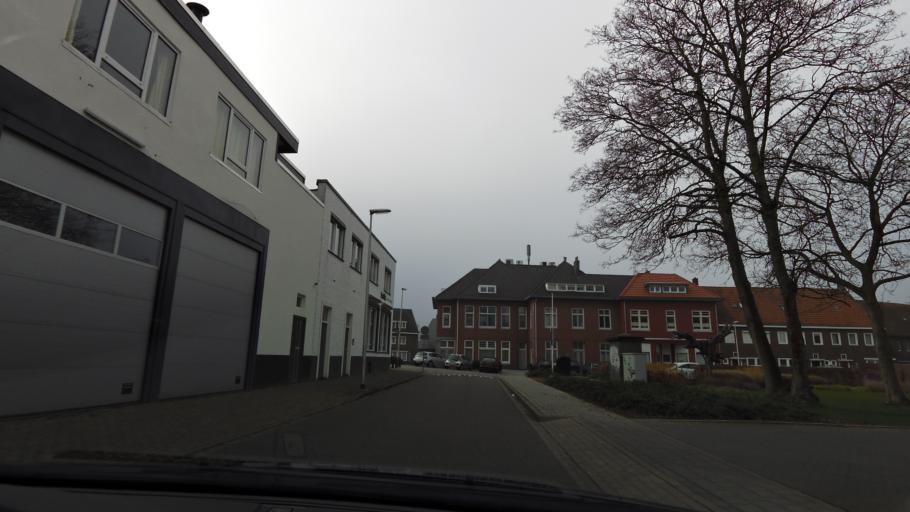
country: NL
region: Limburg
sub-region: Gemeente Heerlen
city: Heerlen
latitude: 50.8851
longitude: 5.9947
